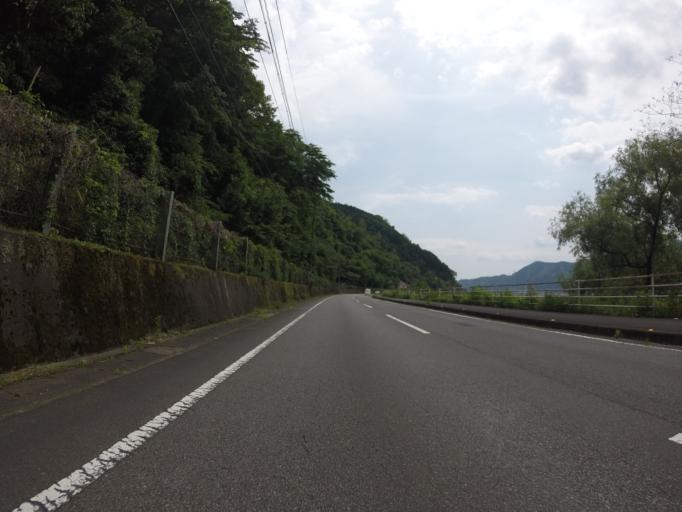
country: JP
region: Shizuoka
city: Shizuoka-shi
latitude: 35.0832
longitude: 138.3763
